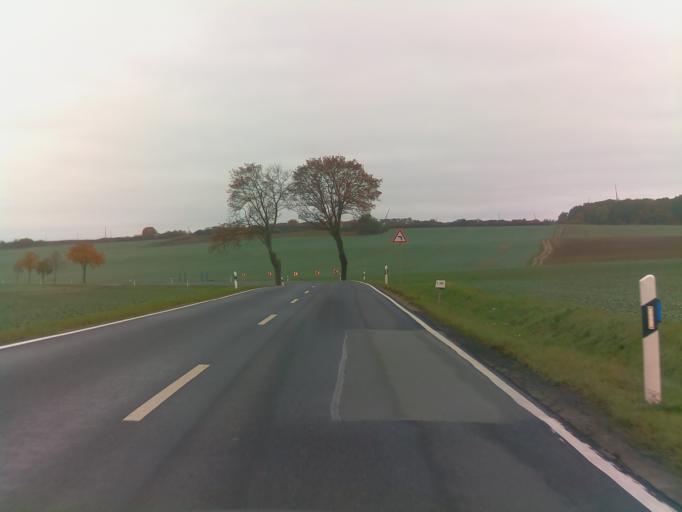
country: DE
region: Thuringia
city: Stadtilm
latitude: 50.7836
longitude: 11.0686
